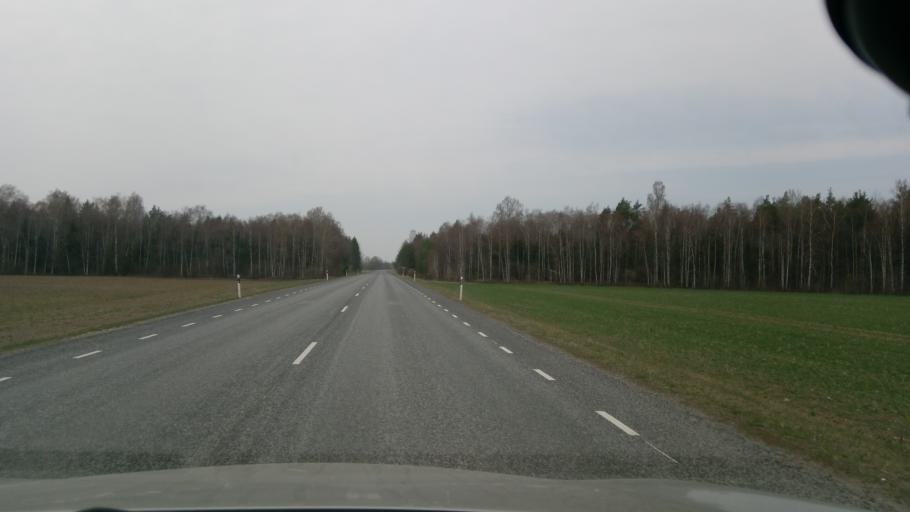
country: EE
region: Jaervamaa
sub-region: Tueri vald
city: Sarevere
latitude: 58.7642
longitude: 25.5412
